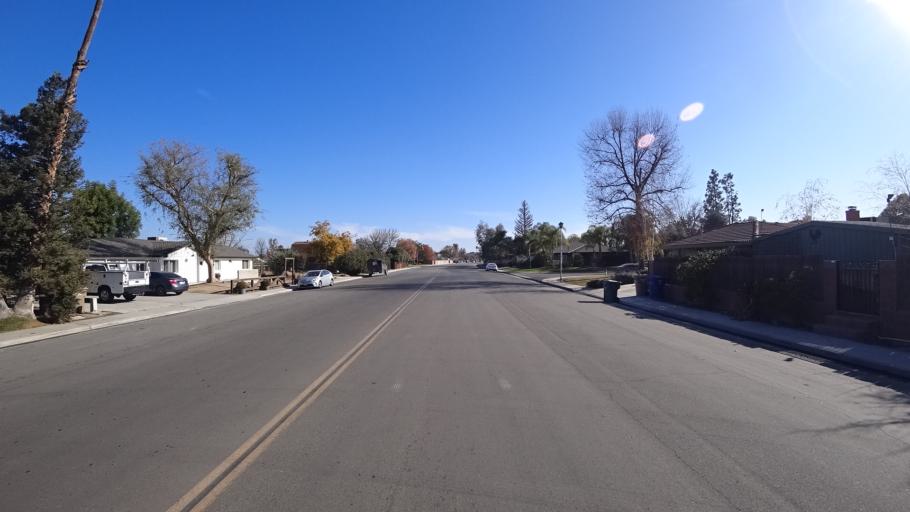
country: US
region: California
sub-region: Kern County
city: Greenacres
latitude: 35.3761
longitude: -119.1232
